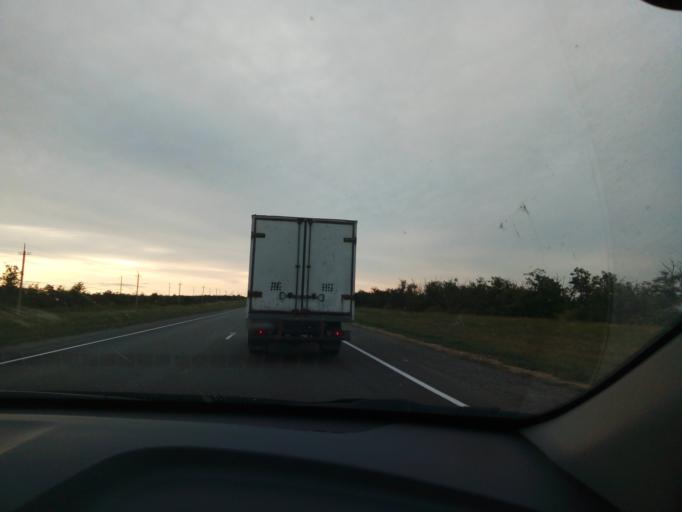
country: RU
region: Volgograd
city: Primorsk
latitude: 49.2269
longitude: 44.9033
